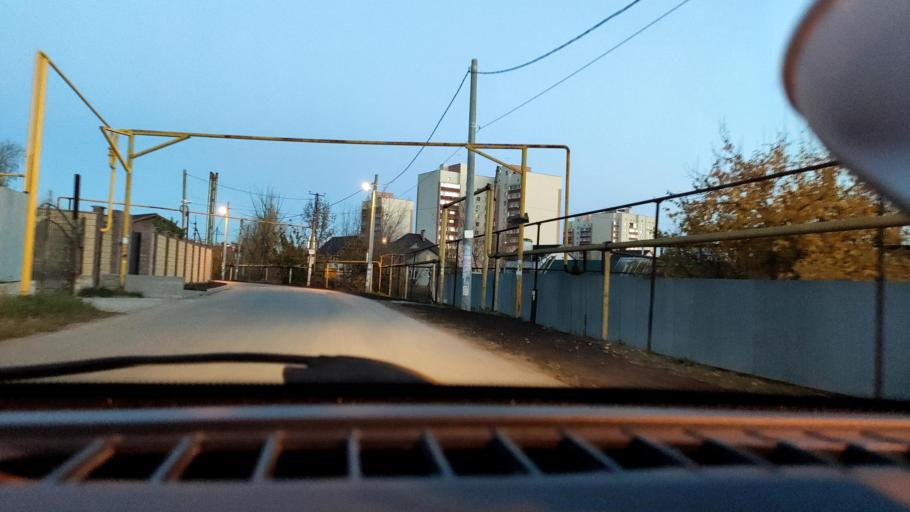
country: RU
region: Samara
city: Samara
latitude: 53.1512
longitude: 50.0859
